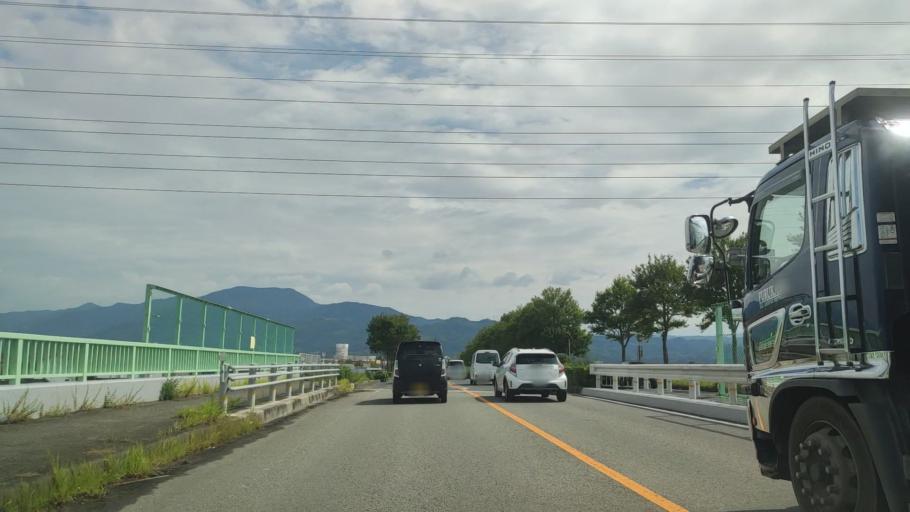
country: JP
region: Wakayama
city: Iwade
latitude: 34.2620
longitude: 135.3372
